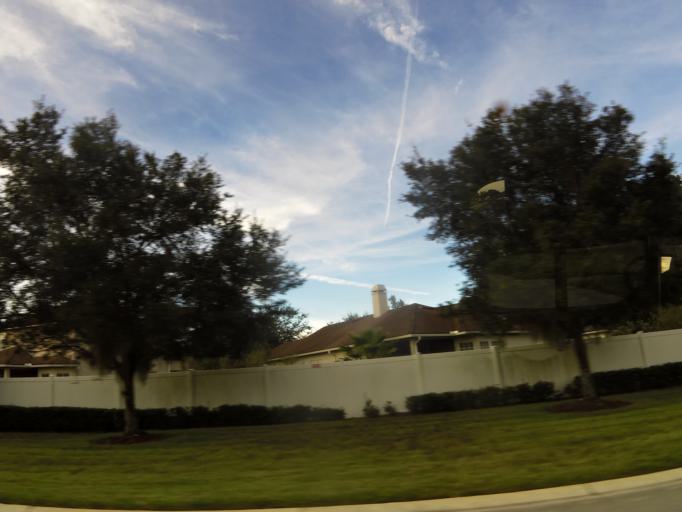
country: US
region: Florida
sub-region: Saint Johns County
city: Fruit Cove
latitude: 30.1493
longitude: -81.5410
